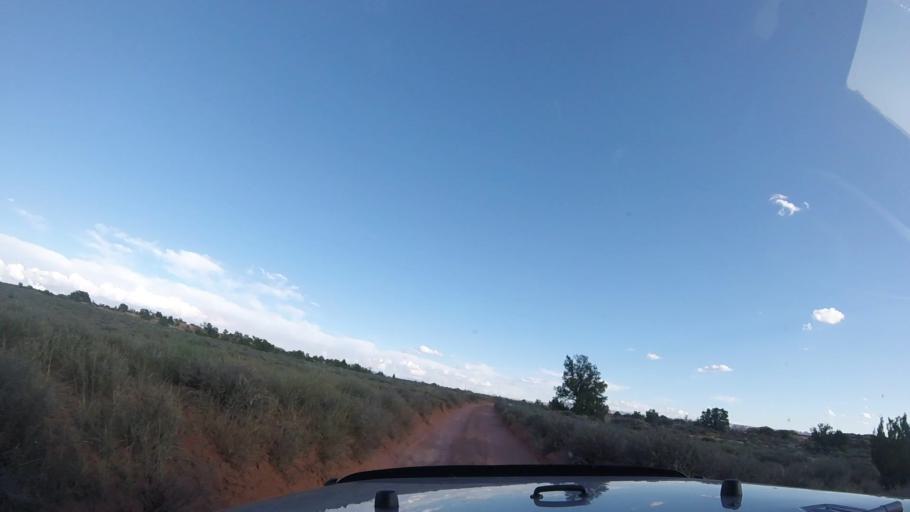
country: US
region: Utah
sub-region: Grand County
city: Moab
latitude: 38.2024
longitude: -109.7832
